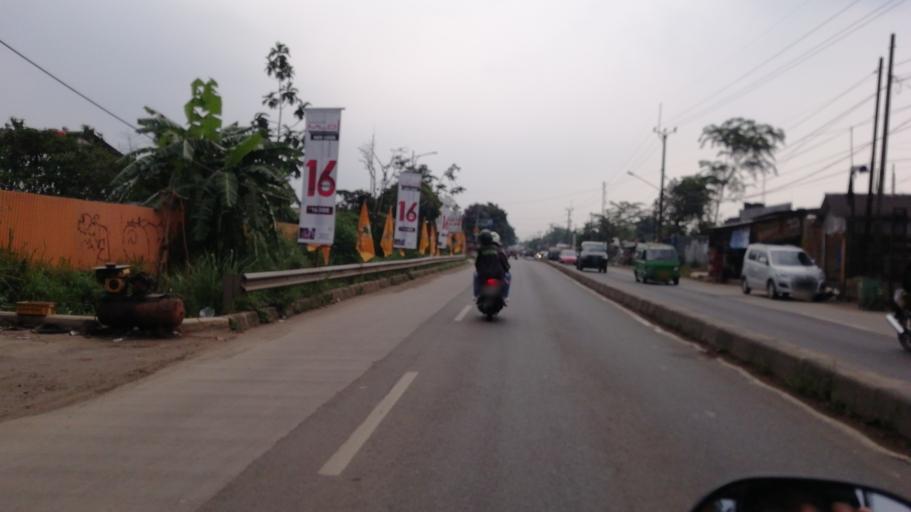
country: ID
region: West Java
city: Ciampea
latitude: -6.5055
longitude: 106.7578
